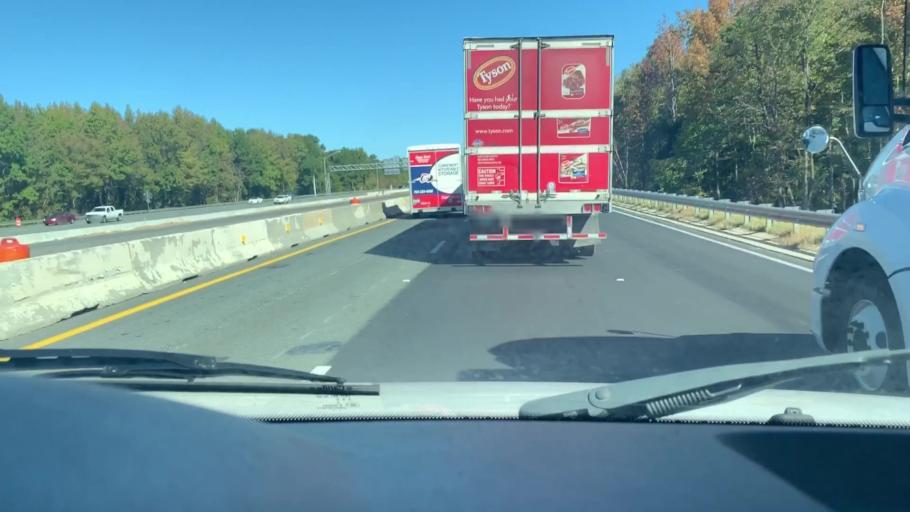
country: US
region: North Carolina
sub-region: Mecklenburg County
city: Huntersville
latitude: 35.3411
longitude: -80.8484
